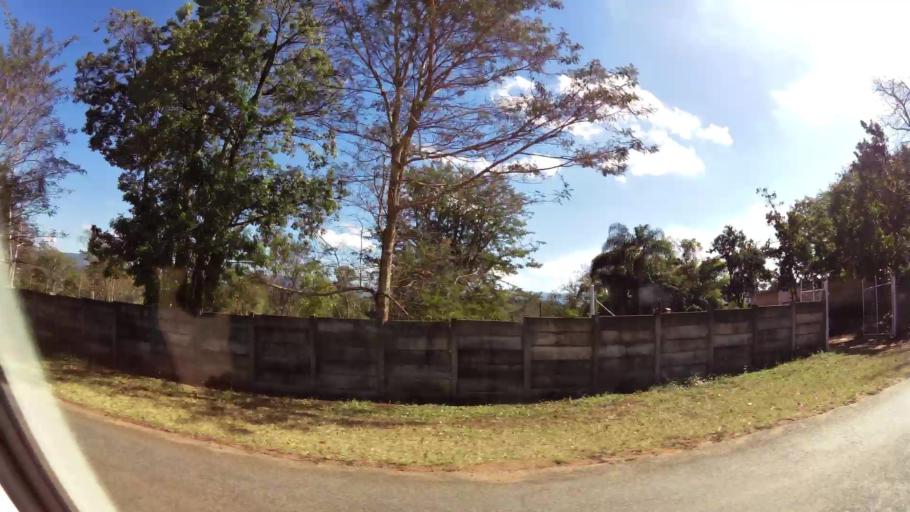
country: ZA
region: Limpopo
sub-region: Mopani District Municipality
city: Tzaneen
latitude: -23.8214
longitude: 30.1688
